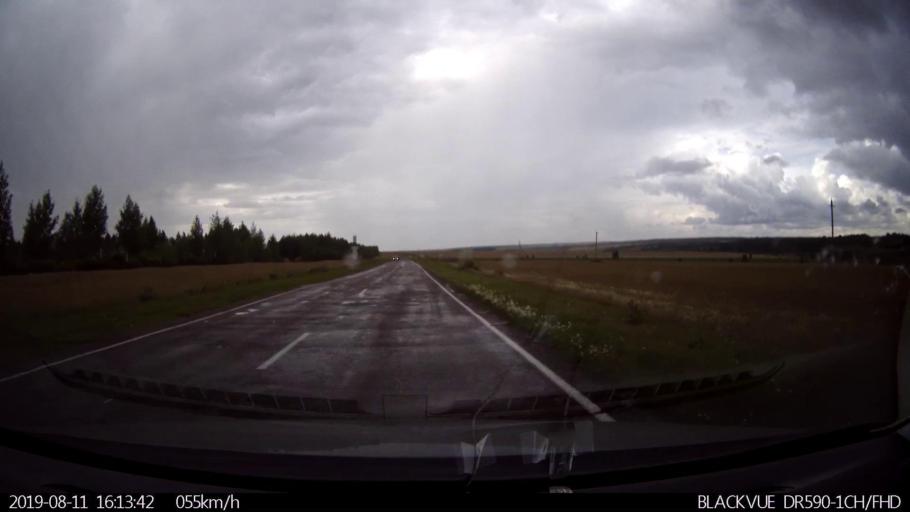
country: RU
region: Ulyanovsk
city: Ignatovka
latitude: 54.0222
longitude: 47.6361
